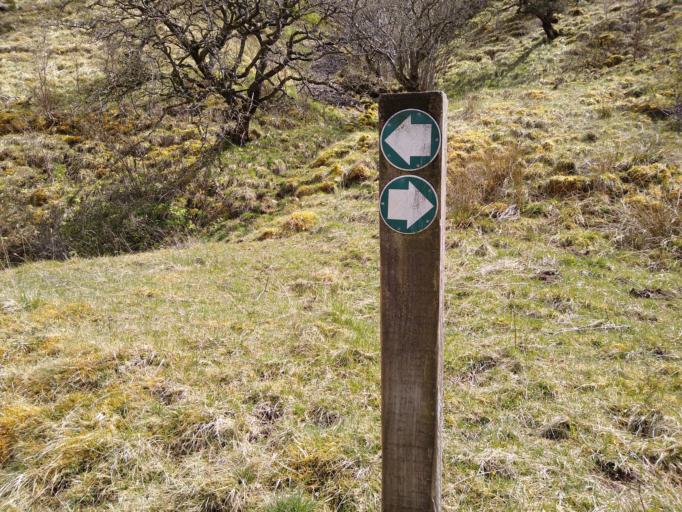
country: GB
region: England
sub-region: Cumbria
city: Kirkby Stephen
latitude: 54.4525
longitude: -2.4246
